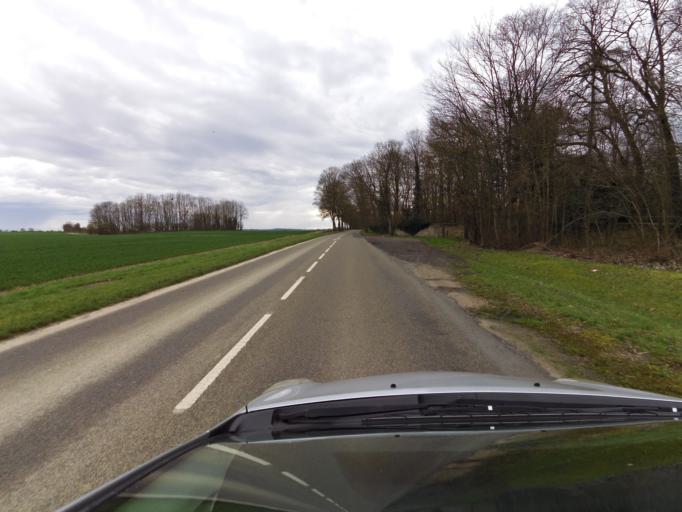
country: FR
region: Picardie
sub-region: Departement de l'Oise
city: Chamant
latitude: 49.1985
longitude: 2.6122
